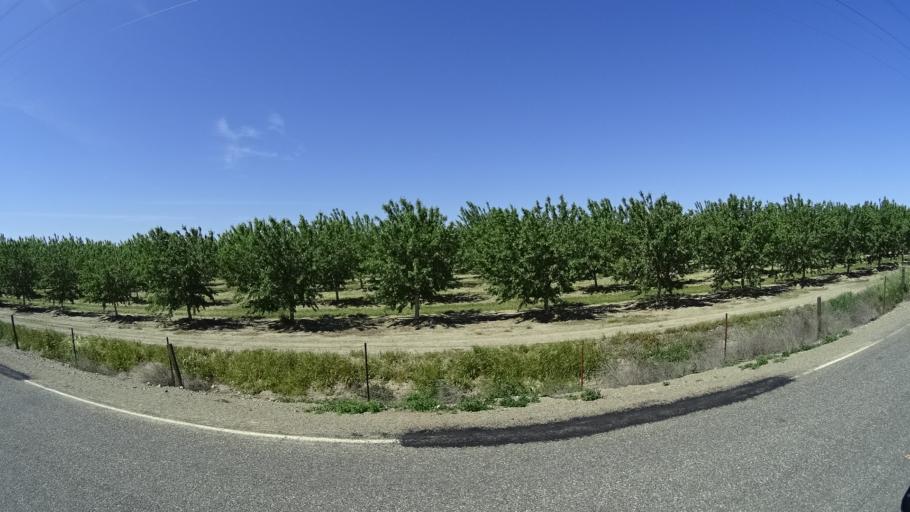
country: US
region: California
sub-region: Glenn County
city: Orland
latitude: 39.6725
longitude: -122.1782
